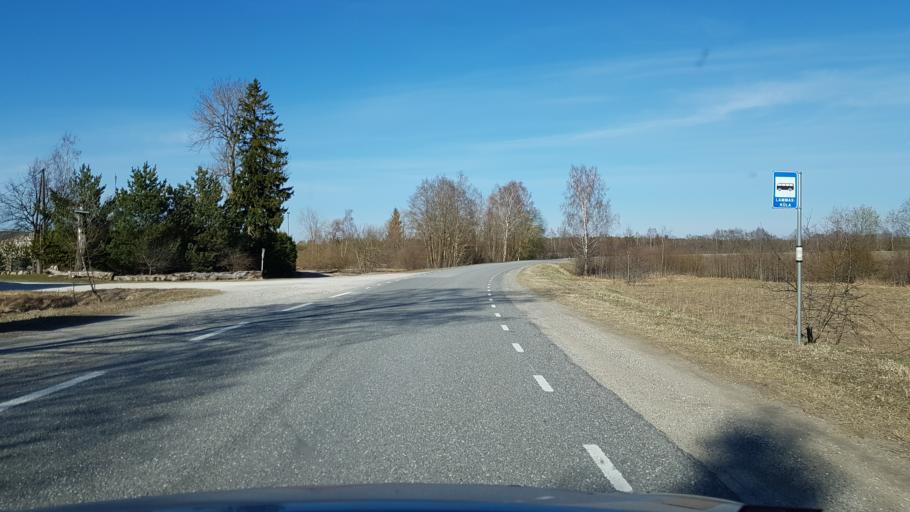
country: EE
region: Laeaene-Virumaa
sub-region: Rakke vald
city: Rakke
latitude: 58.9978
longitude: 26.2746
